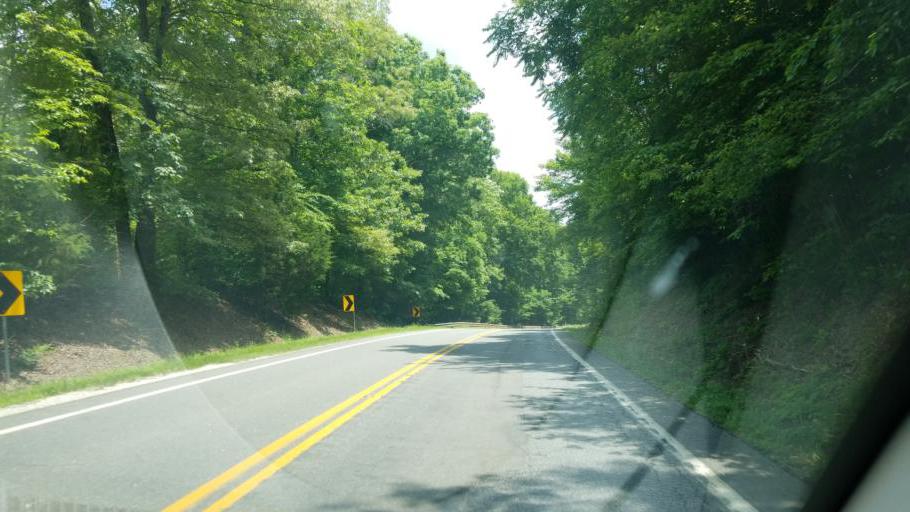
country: US
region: Virginia
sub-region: Amherst County
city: Amherst
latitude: 37.5618
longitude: -78.9783
